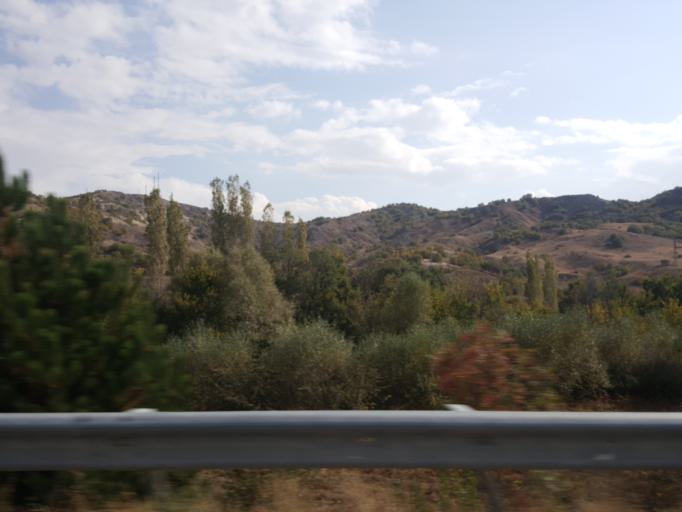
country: TR
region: Corum
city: Sungurlu
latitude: 40.2005
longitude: 34.5155
